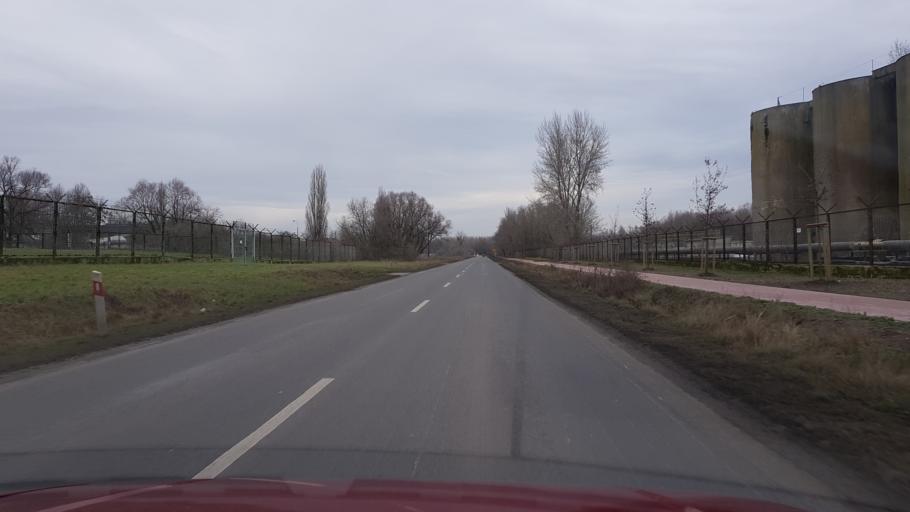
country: PL
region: West Pomeranian Voivodeship
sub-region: Powiat policki
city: Police
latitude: 53.5788
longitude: 14.5539
